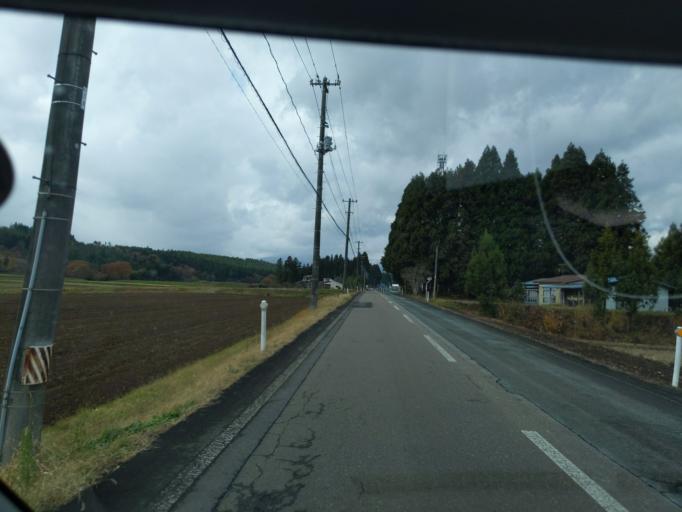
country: JP
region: Iwate
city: Mizusawa
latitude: 39.0850
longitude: 141.0275
